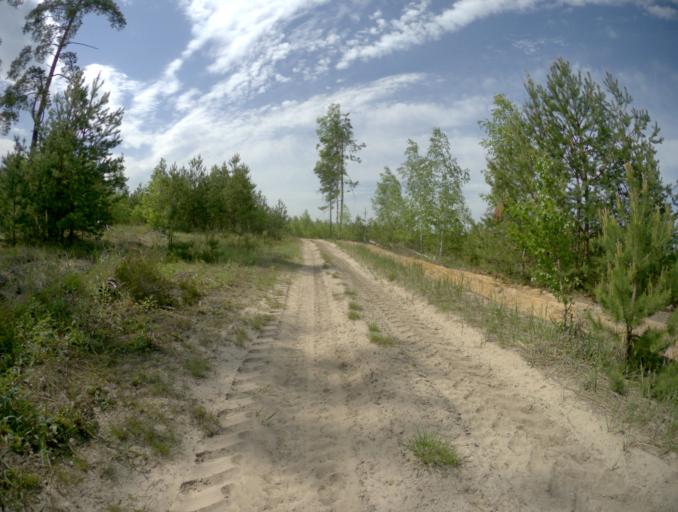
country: RU
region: Vladimir
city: Ivanishchi
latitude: 55.7051
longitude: 40.4441
